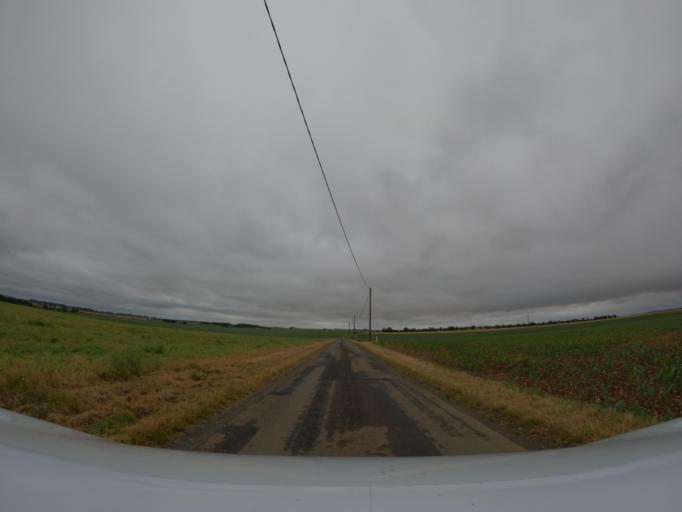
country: FR
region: Pays de la Loire
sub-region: Departement de la Vendee
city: Maillezais
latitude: 46.4190
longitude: -0.7197
